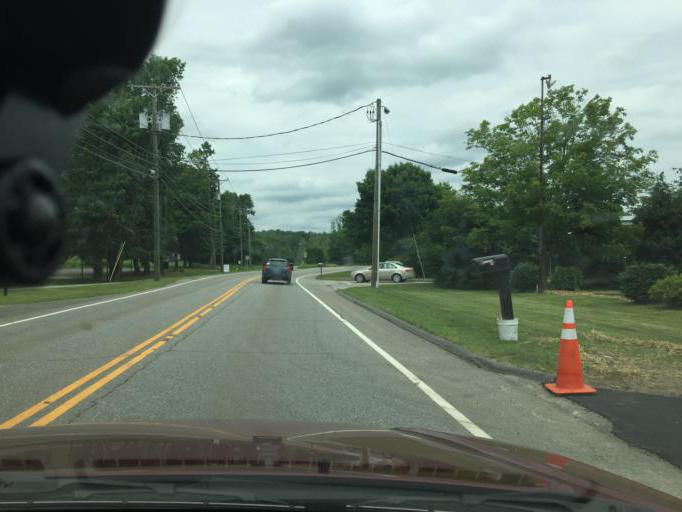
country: US
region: Connecticut
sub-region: Litchfield County
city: Litchfield
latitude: 41.7387
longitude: -73.2158
